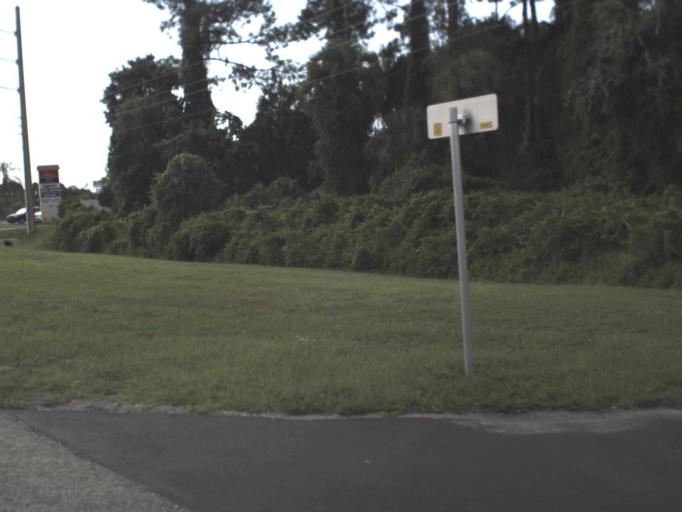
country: US
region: Florida
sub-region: Charlotte County
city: Port Charlotte
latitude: 27.0180
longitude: -82.1579
